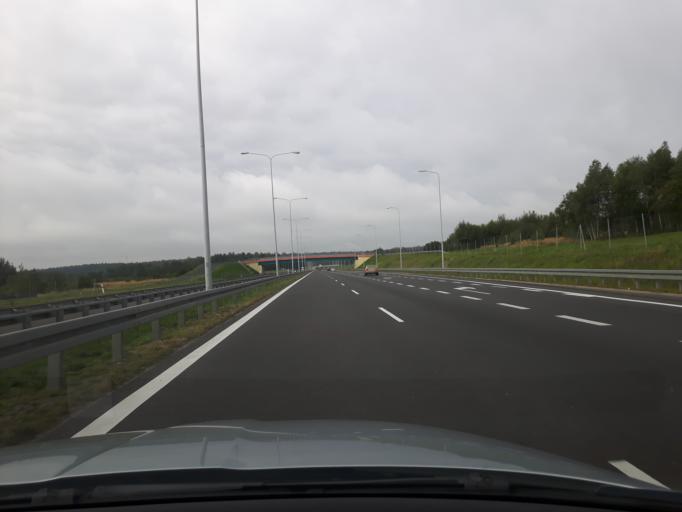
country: PL
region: Swietokrzyskie
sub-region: Powiat kielecki
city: Zagnansk
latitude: 50.9447
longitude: 20.6806
